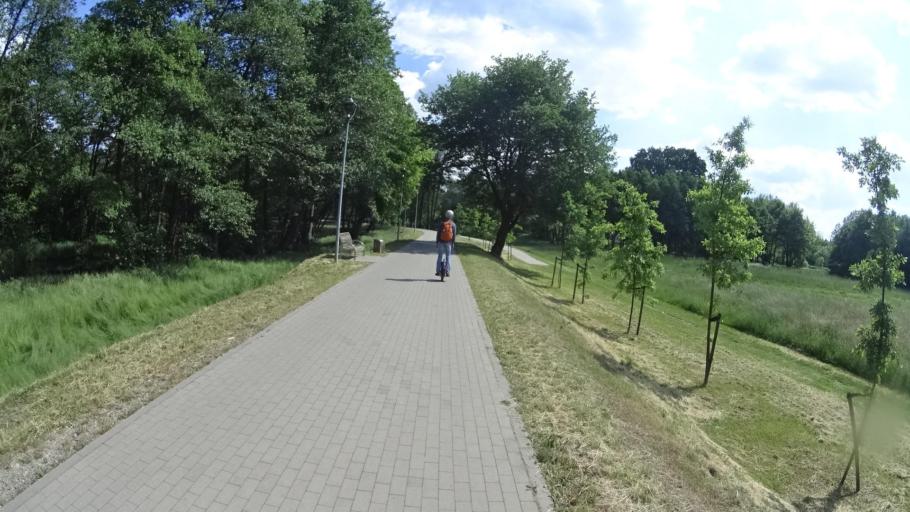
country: PL
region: Masovian Voivodeship
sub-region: Powiat piaseczynski
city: Konstancin-Jeziorna
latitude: 52.0880
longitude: 21.1100
